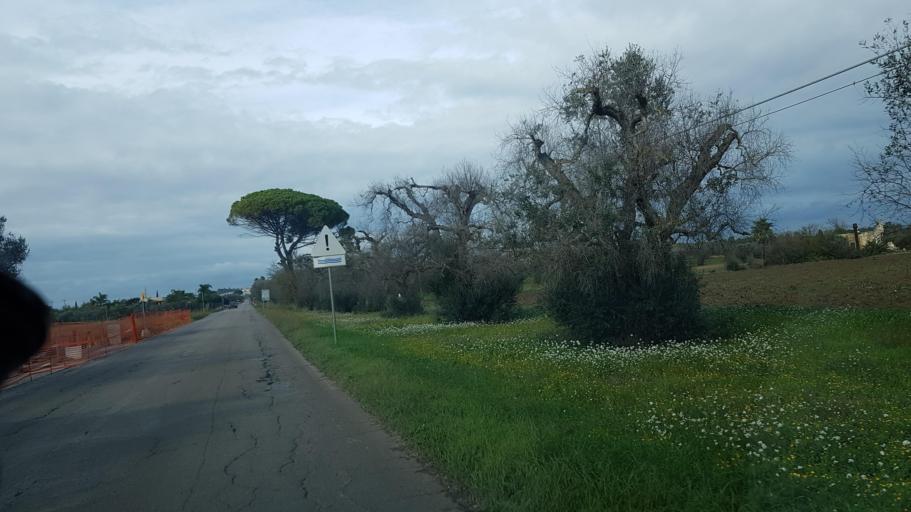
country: IT
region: Apulia
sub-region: Provincia di Brindisi
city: Oria
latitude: 40.4878
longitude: 17.6684
